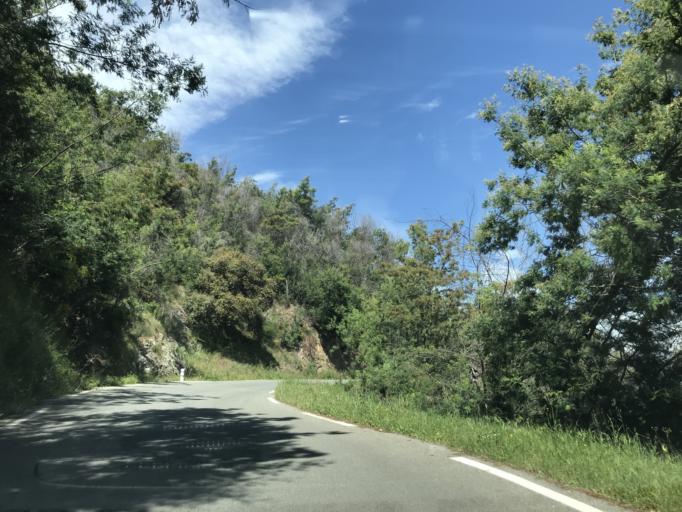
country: FR
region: Provence-Alpes-Cote d'Azur
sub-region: Departement du Var
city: Tanneron
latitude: 43.5864
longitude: 6.8851
